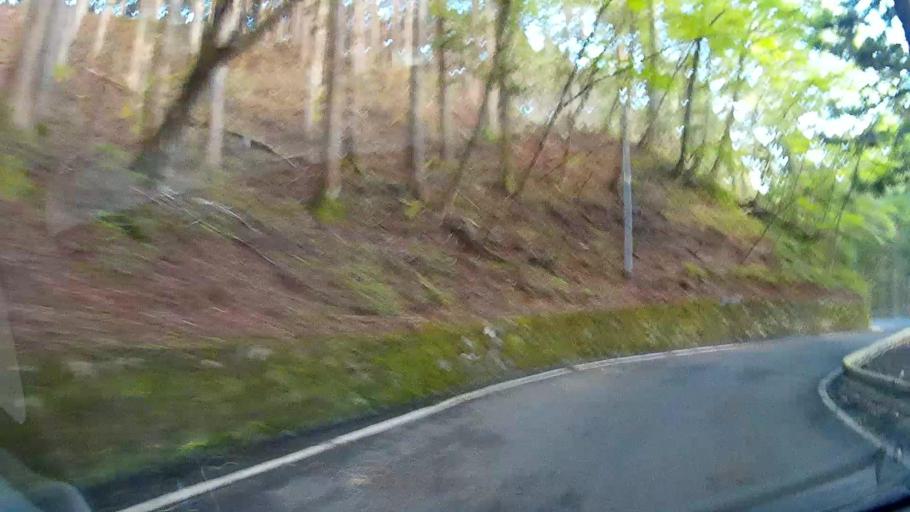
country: JP
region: Shizuoka
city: Shizuoka-shi
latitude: 35.1588
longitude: 138.2656
